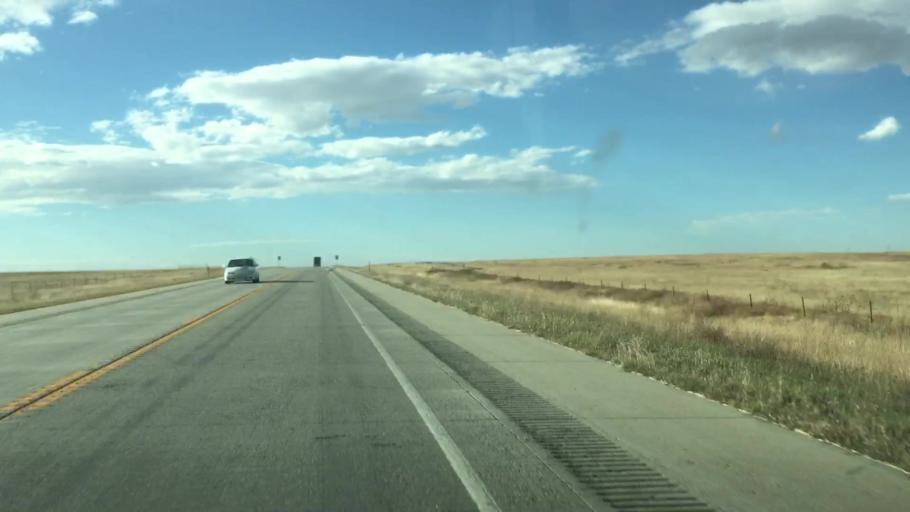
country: US
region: Colorado
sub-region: Lincoln County
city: Hugo
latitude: 39.1853
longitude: -103.5533
